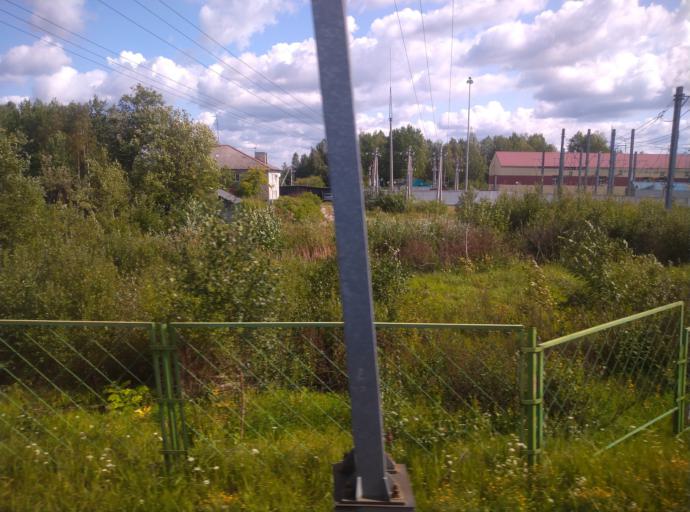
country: RU
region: Leningrad
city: Krasnyy Bor
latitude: 59.6770
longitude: 30.7059
